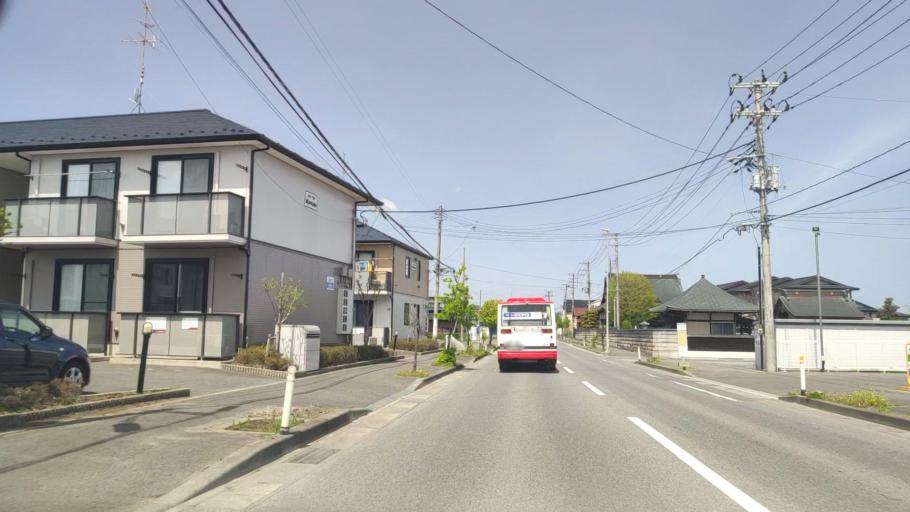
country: JP
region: Aomori
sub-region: Hachinohe Shi
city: Uchimaru
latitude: 40.5042
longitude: 141.4395
